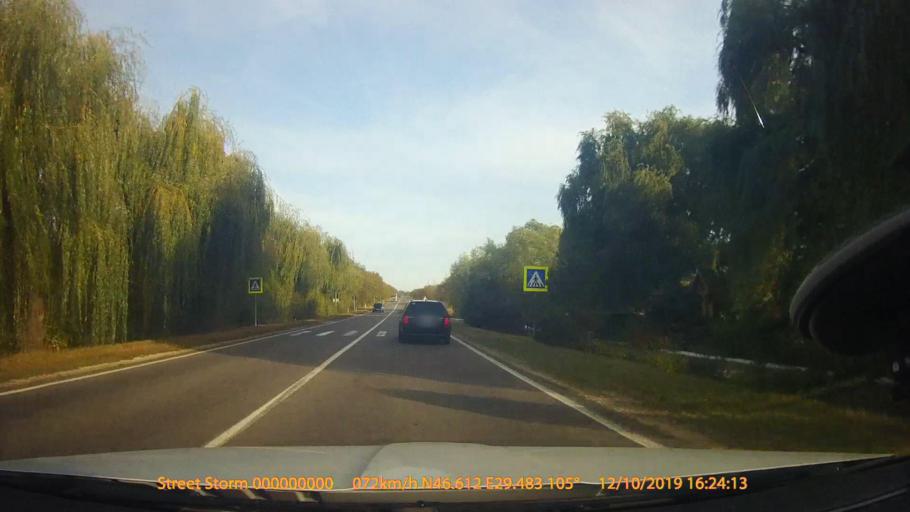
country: MD
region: Causeni
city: Causeni
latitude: 46.6122
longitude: 29.4832
